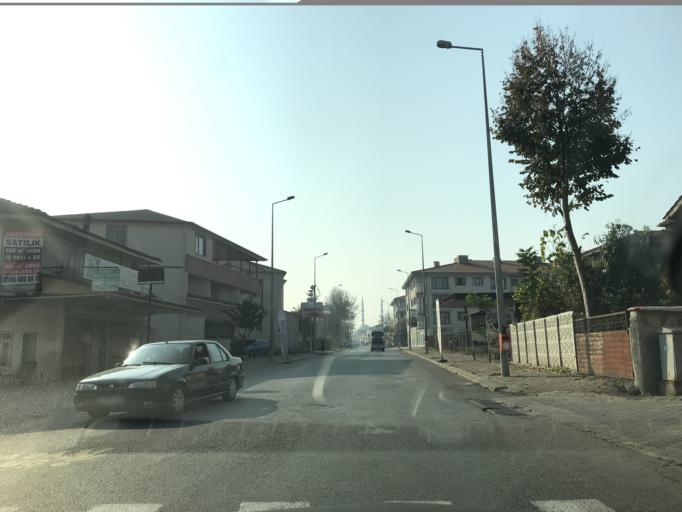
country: TR
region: Duzce
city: Cumayeri
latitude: 40.8816
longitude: 30.9513
